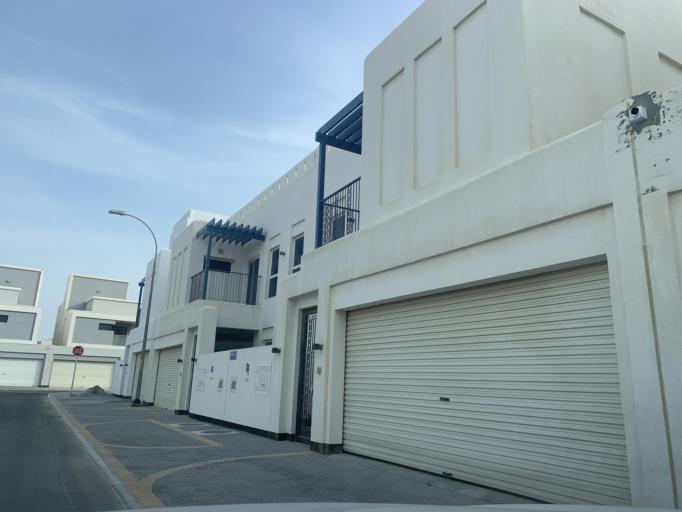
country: BH
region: Muharraq
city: Al Muharraq
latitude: 26.3161
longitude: 50.6298
